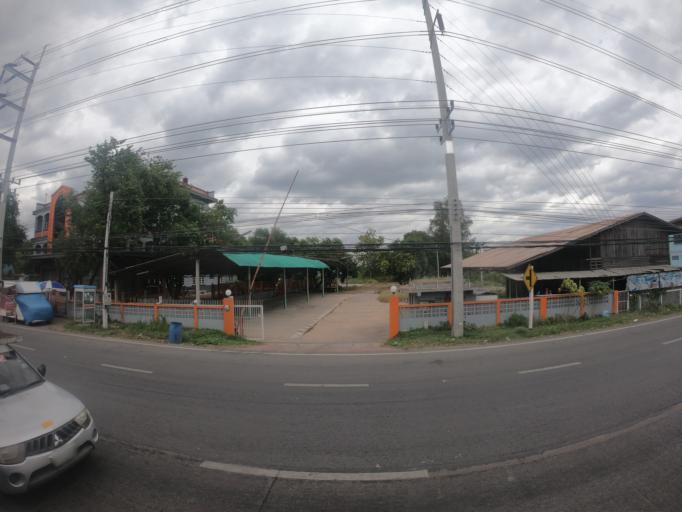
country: TH
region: Nakhon Ratchasima
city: Nakhon Ratchasima
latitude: 14.9316
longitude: 102.1377
